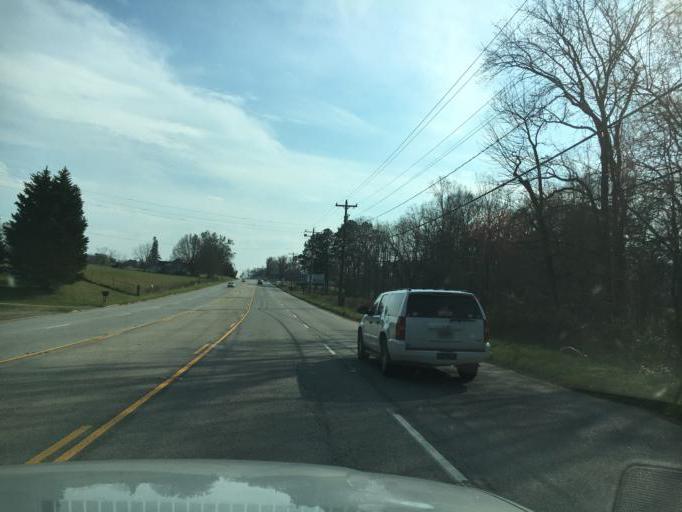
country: US
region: South Carolina
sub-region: Spartanburg County
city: Mayo
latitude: 35.0364
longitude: -81.8944
